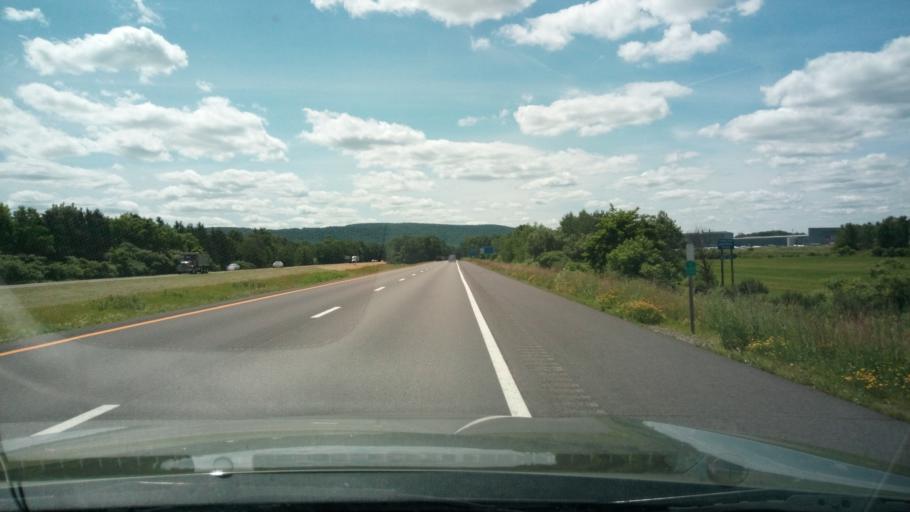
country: US
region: Pennsylvania
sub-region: Bradford County
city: South Waverly
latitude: 42.0013
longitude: -76.6075
